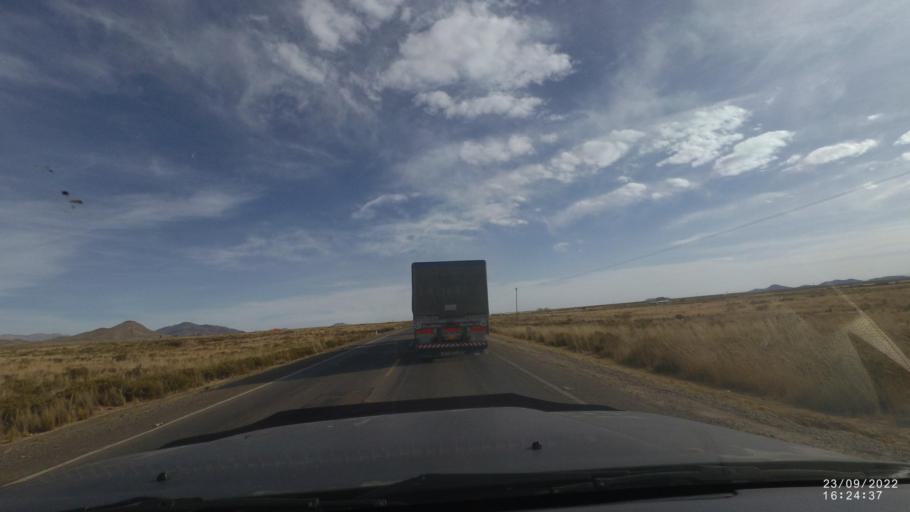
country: BO
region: Oruro
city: Machacamarca
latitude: -18.0843
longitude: -67.0087
